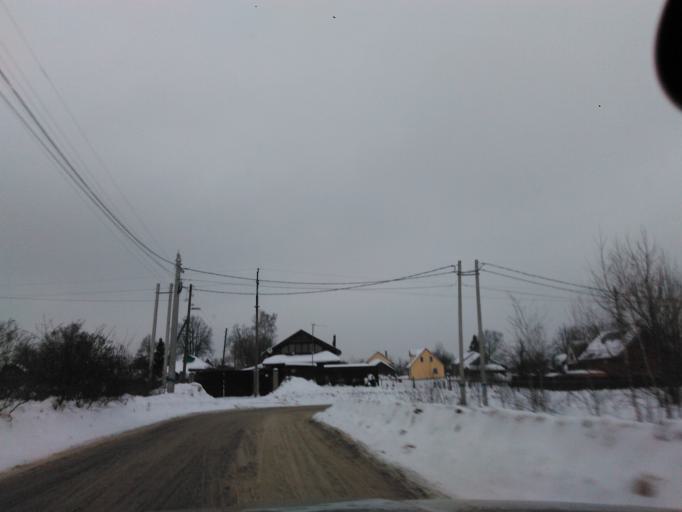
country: RU
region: Moskovskaya
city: Yakhroma
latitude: 56.2695
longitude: 37.4534
